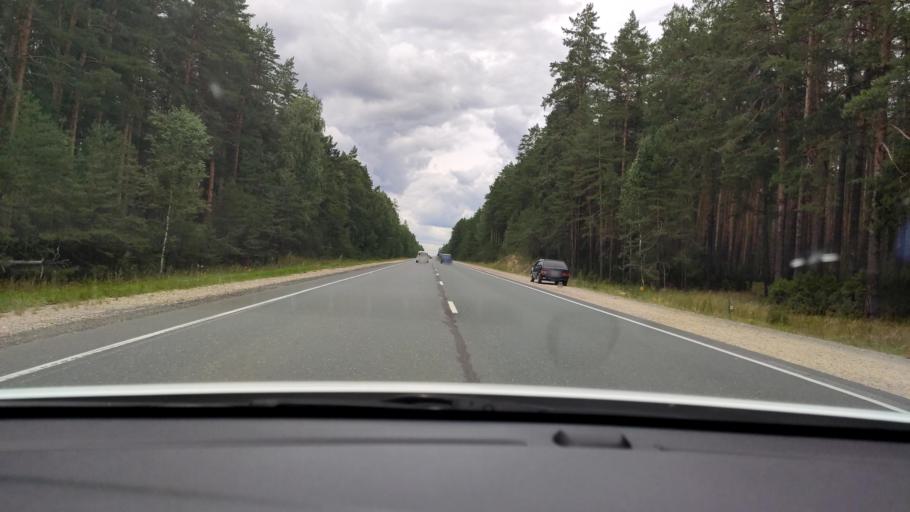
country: RU
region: Mariy-El
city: Pomary
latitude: 56.0324
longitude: 48.3816
